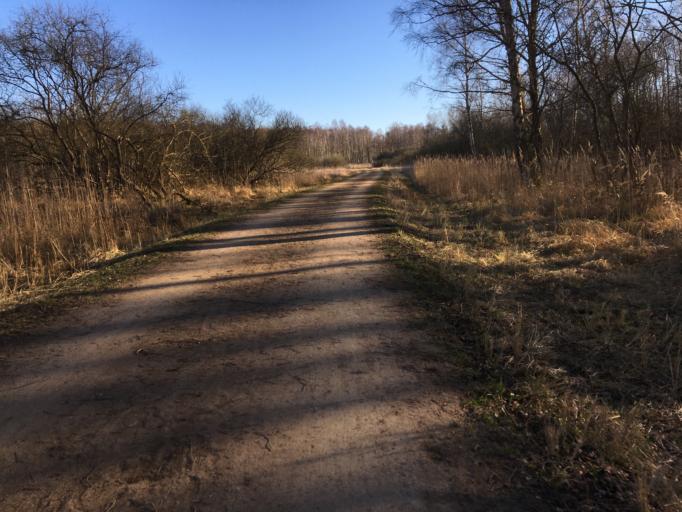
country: DK
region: Capital Region
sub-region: Tarnby Kommune
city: Tarnby
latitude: 55.5928
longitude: 12.5565
